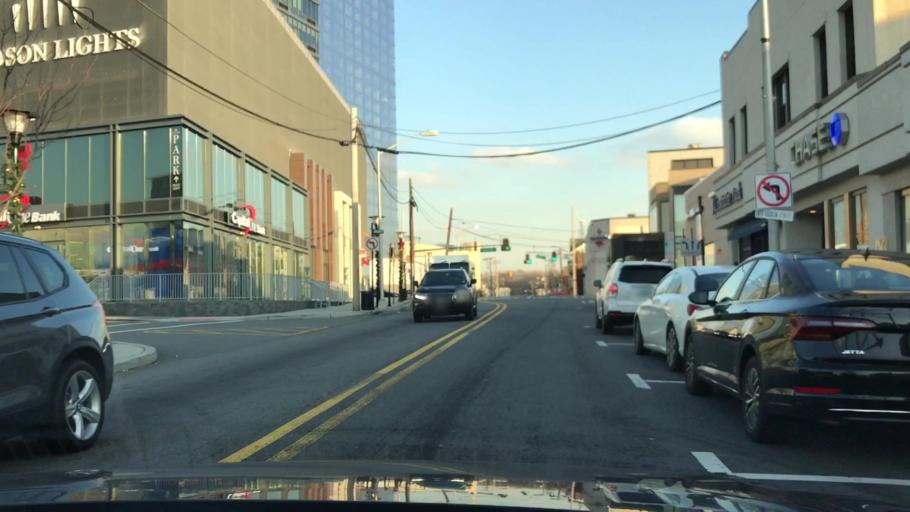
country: US
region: New Jersey
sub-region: Bergen County
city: Fort Lee
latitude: 40.8511
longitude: -73.9696
